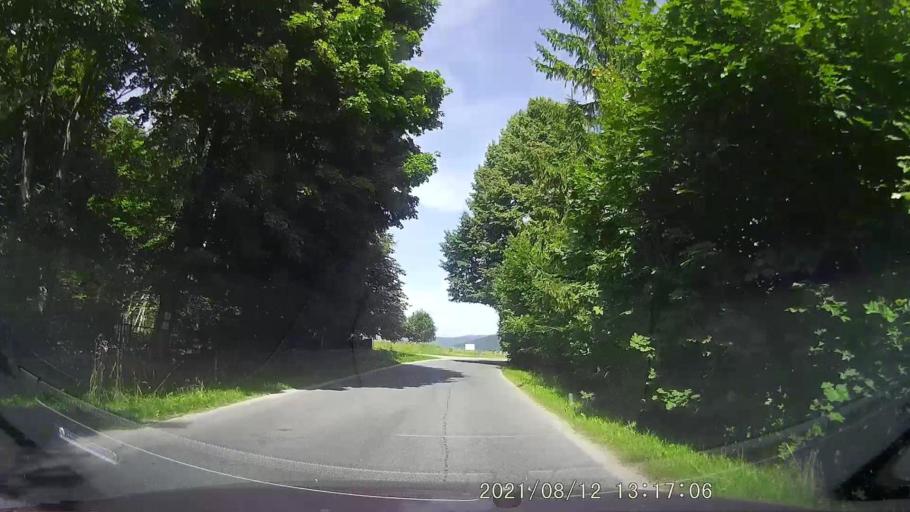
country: PL
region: Lower Silesian Voivodeship
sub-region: Powiat klodzki
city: Stronie Slaskie
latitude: 50.2680
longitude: 16.8810
